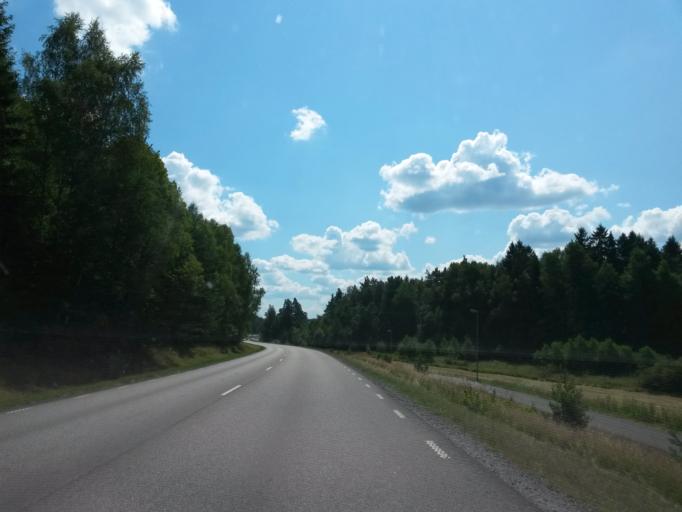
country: SE
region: Vaestra Goetaland
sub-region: Lerums Kommun
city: Stenkullen
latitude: 57.8090
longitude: 12.3022
